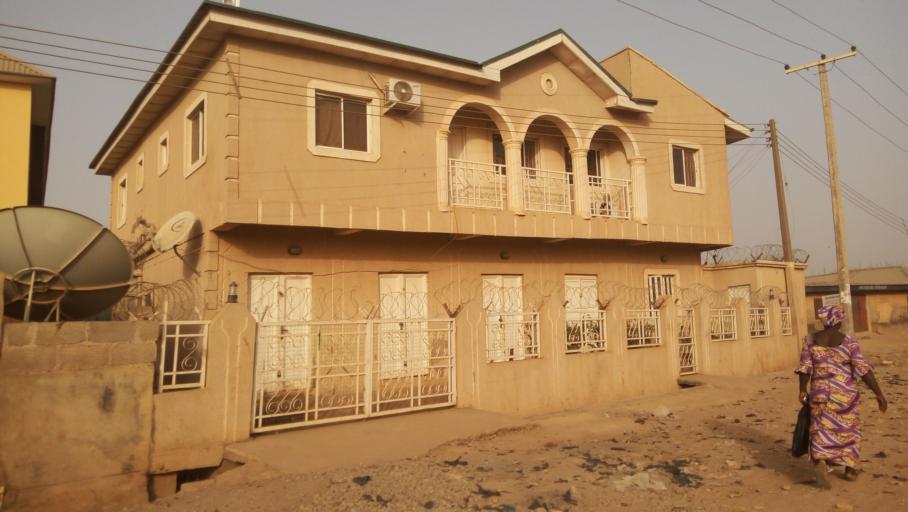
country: NG
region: Kaduna
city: Zaria
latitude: 11.1621
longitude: 7.6548
